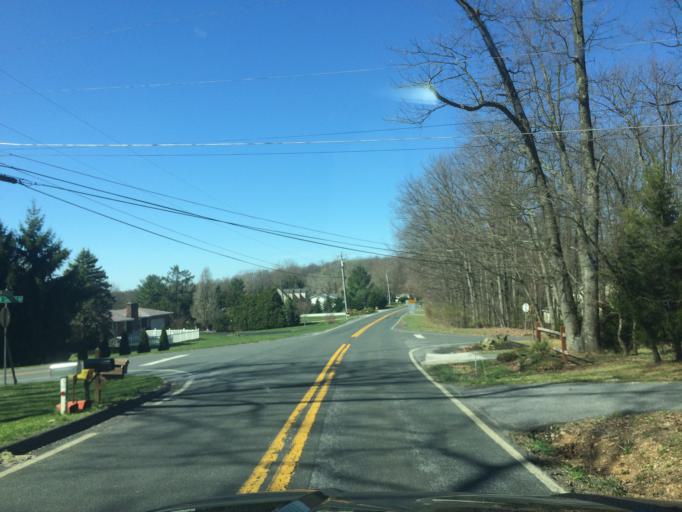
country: US
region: Maryland
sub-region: Carroll County
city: Manchester
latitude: 39.6852
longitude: -76.9723
